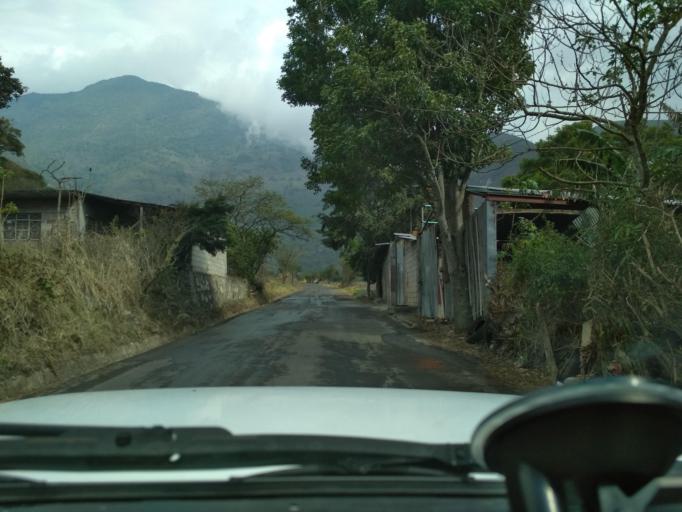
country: MX
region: Veracruz
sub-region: Nogales
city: Taza de Agua Ojo Zarco
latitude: 18.7814
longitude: -97.2002
